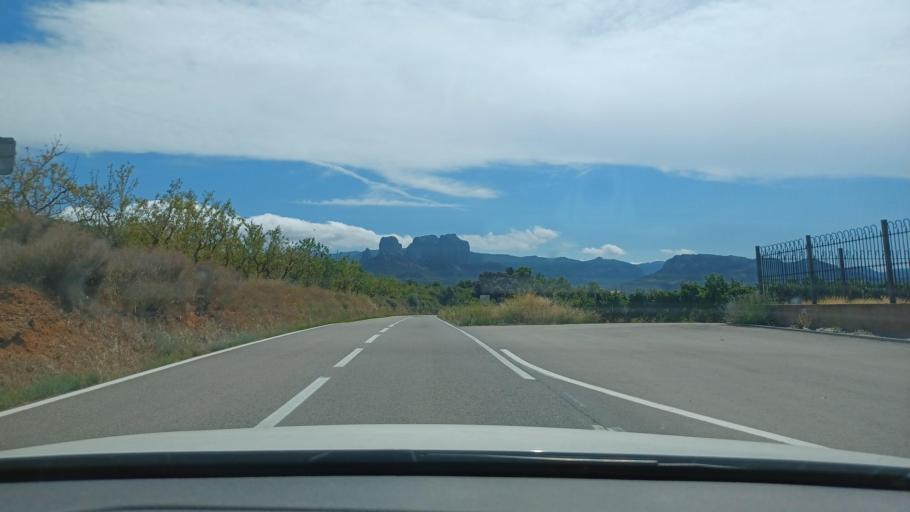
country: ES
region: Catalonia
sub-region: Provincia de Tarragona
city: Horta de Sant Joan
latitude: 40.9417
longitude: 0.3163
